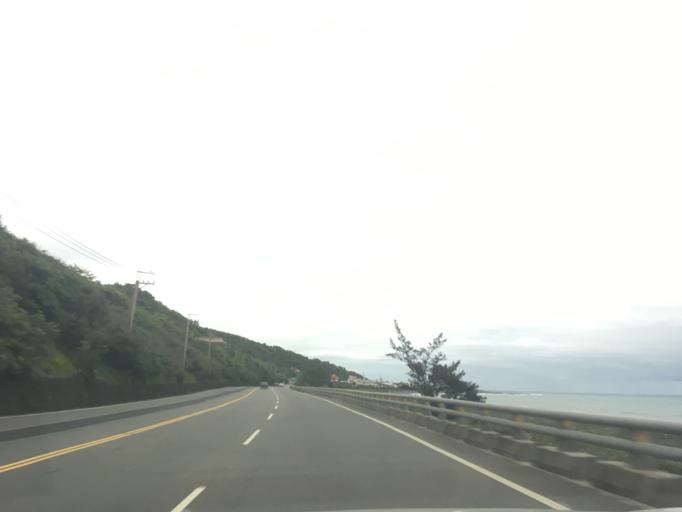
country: TW
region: Taiwan
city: Hengchun
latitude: 22.3482
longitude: 120.9001
